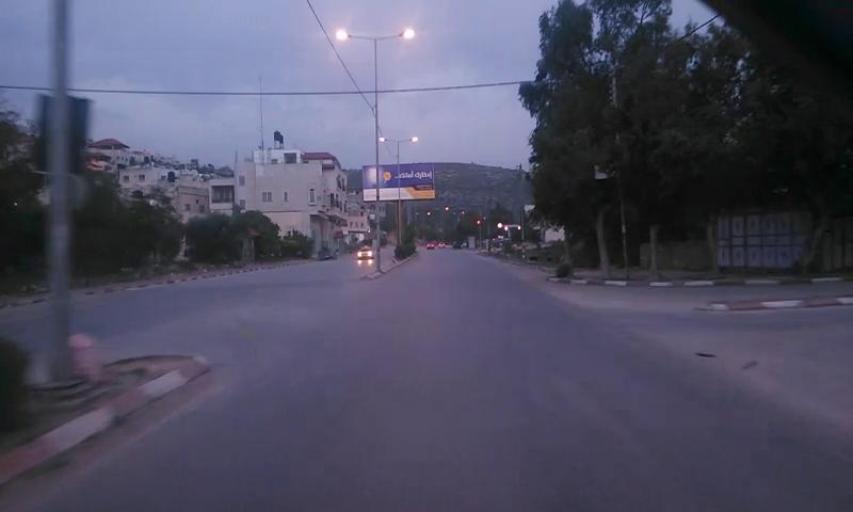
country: PS
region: West Bank
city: `Anabta
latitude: 32.3041
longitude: 35.1255
